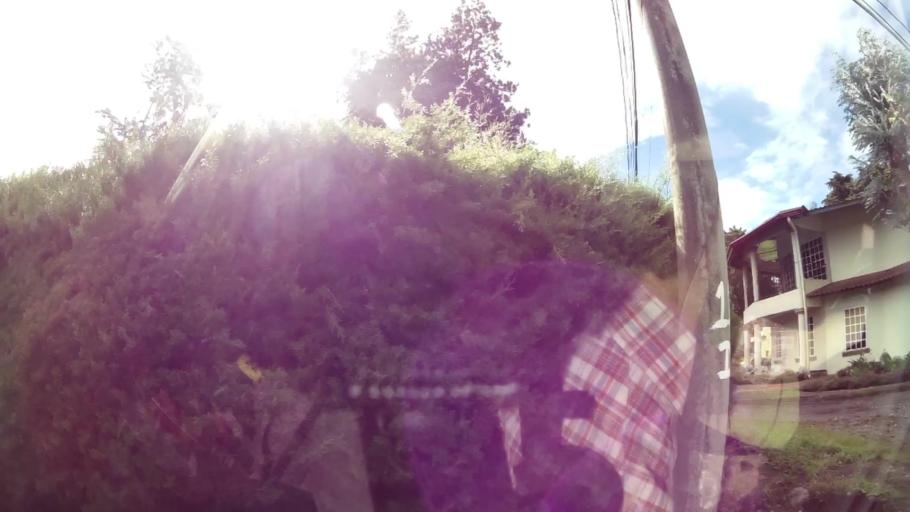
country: PA
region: Chiriqui
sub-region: Distrito Boquete
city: Boquete
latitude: 8.7983
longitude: -82.4338
